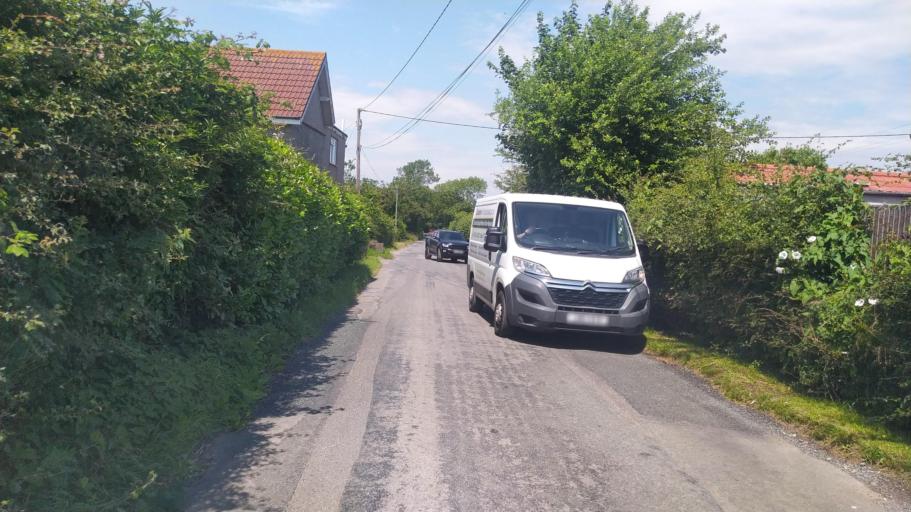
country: GB
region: England
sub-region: North Somerset
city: Banwell
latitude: 51.3326
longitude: -2.8884
